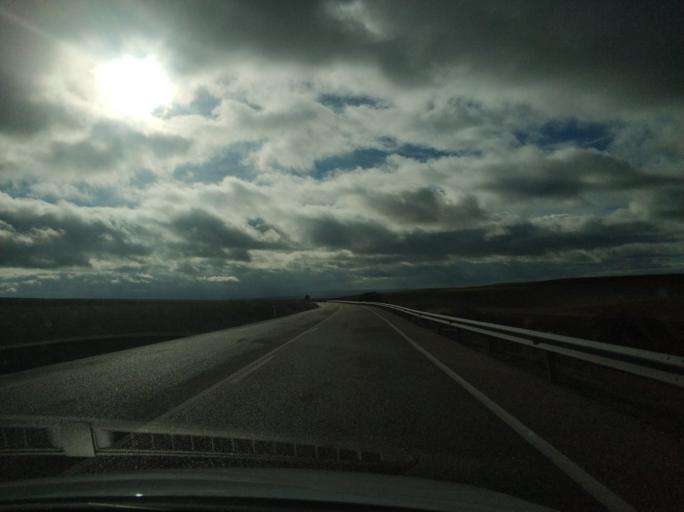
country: ES
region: Castille and Leon
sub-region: Provincia de Soria
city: Fuentecambron
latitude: 41.4578
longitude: -3.3346
